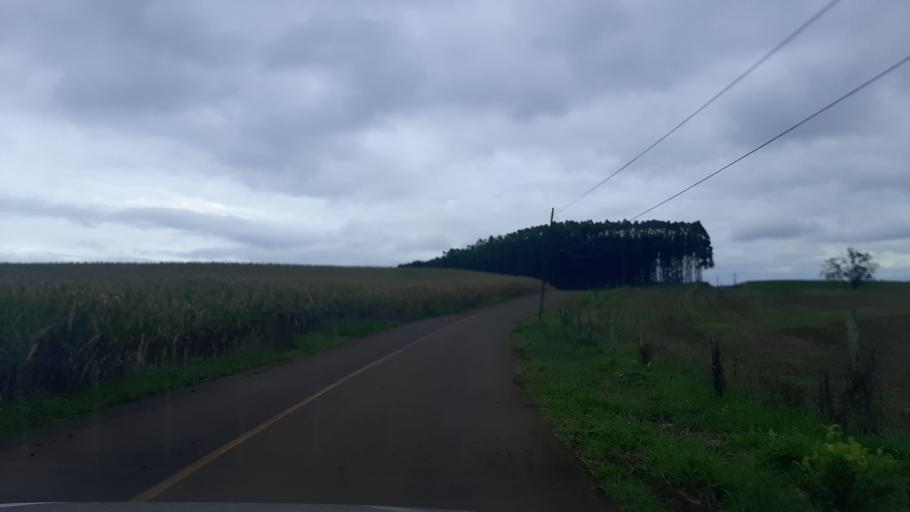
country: BR
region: Parana
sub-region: Ampere
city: Ampere
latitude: -26.0420
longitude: -53.4984
